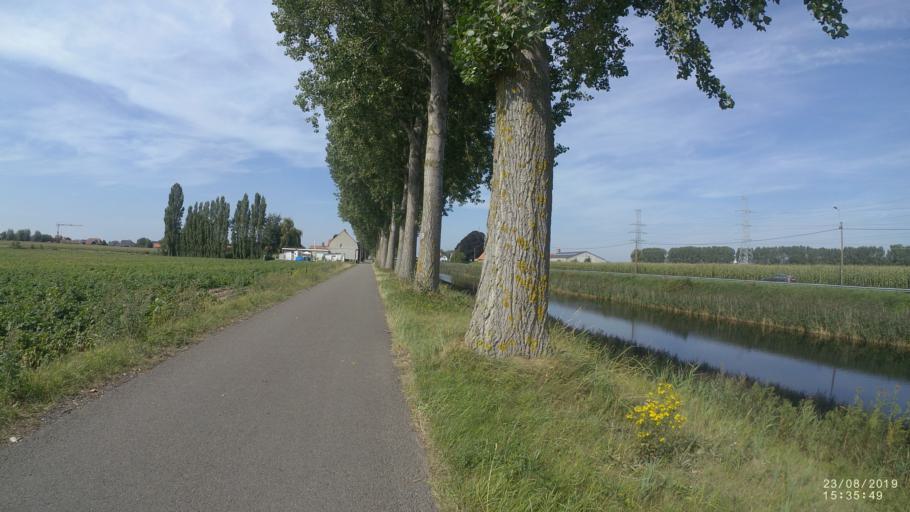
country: BE
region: Flanders
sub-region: Provincie Oost-Vlaanderen
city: Eeklo
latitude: 51.1673
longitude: 3.5416
